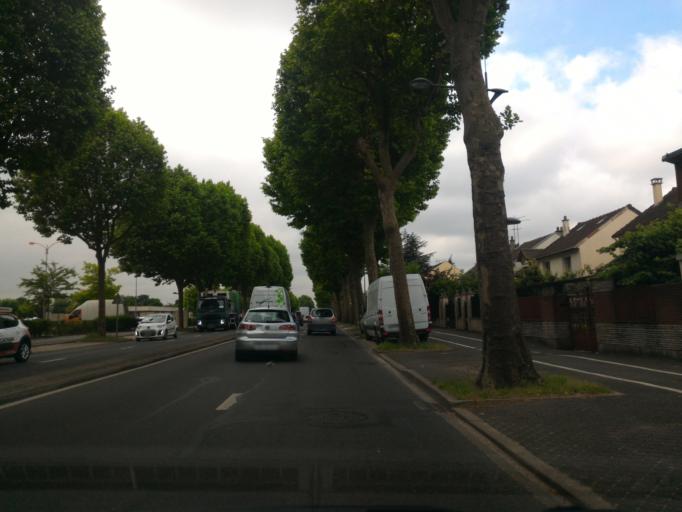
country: FR
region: Ile-de-France
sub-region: Departement du Val-de-Marne
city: Chevilly-Larue
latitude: 48.7692
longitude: 2.3372
